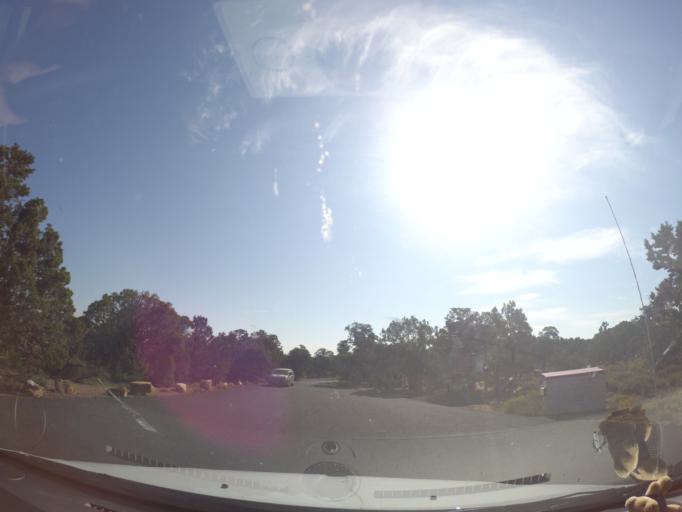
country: US
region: Arizona
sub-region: Coconino County
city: Grand Canyon
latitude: 36.0402
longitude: -111.8231
